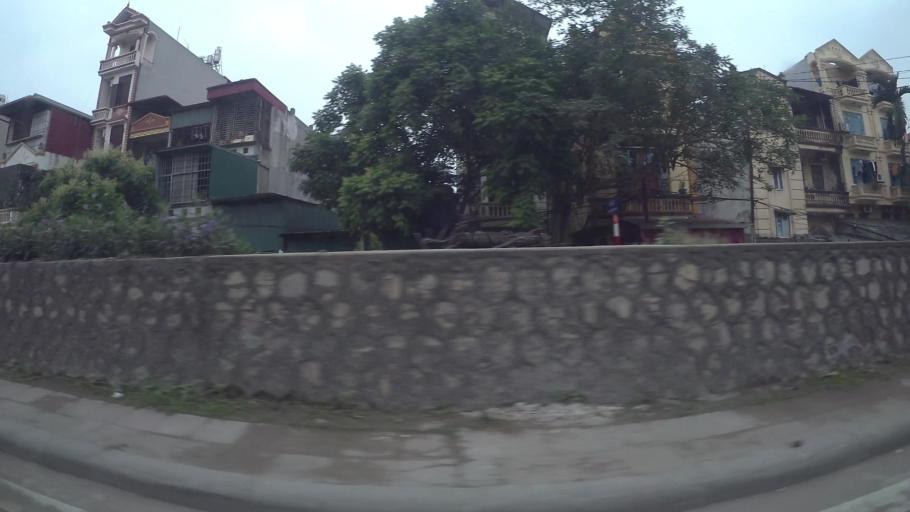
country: VN
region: Ha Noi
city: Hai BaTrung
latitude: 21.0008
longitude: 105.8798
